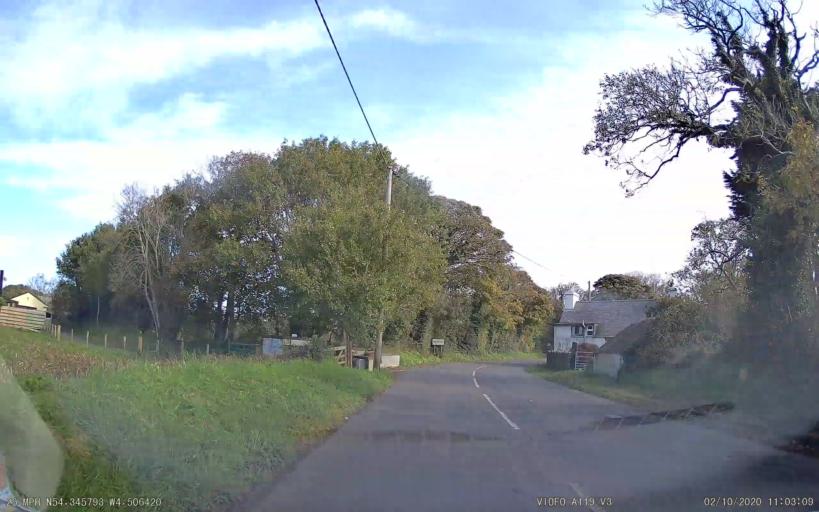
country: IM
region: Ramsey
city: Ramsey
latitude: 54.3458
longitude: -4.5064
